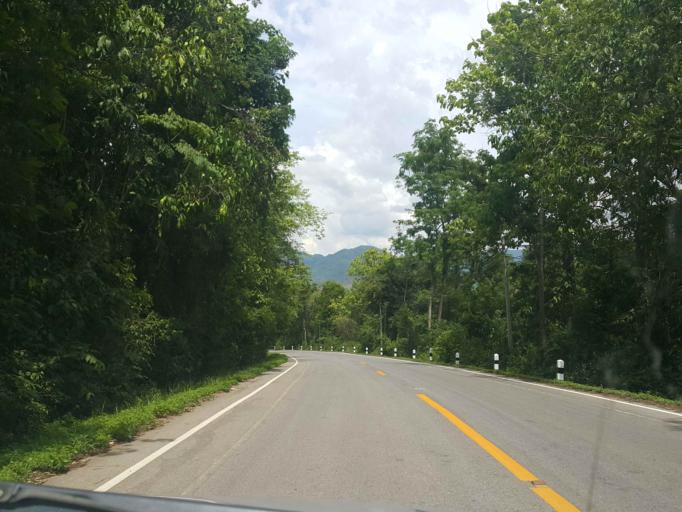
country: TH
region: Nan
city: Ban Luang
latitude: 18.8433
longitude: 100.4141
